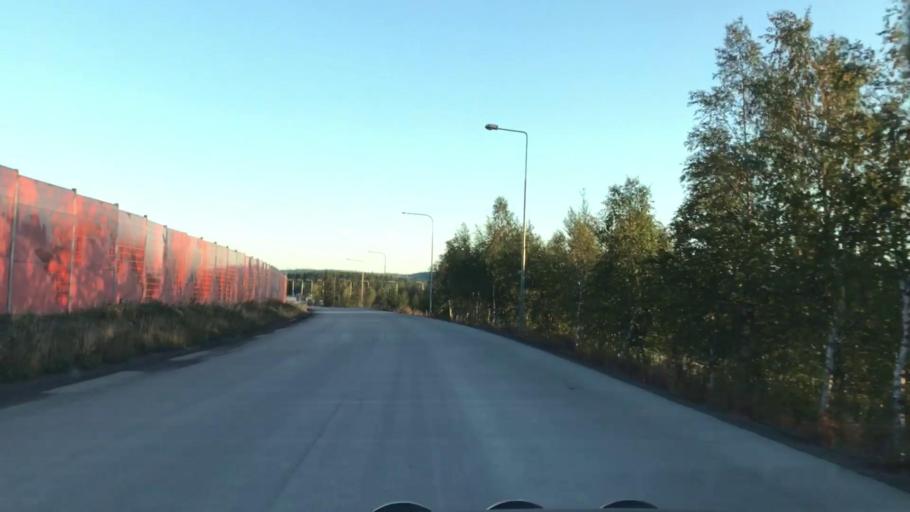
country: SE
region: Norrbotten
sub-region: Gallivare Kommun
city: Malmberget
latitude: 67.6498
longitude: 21.0187
